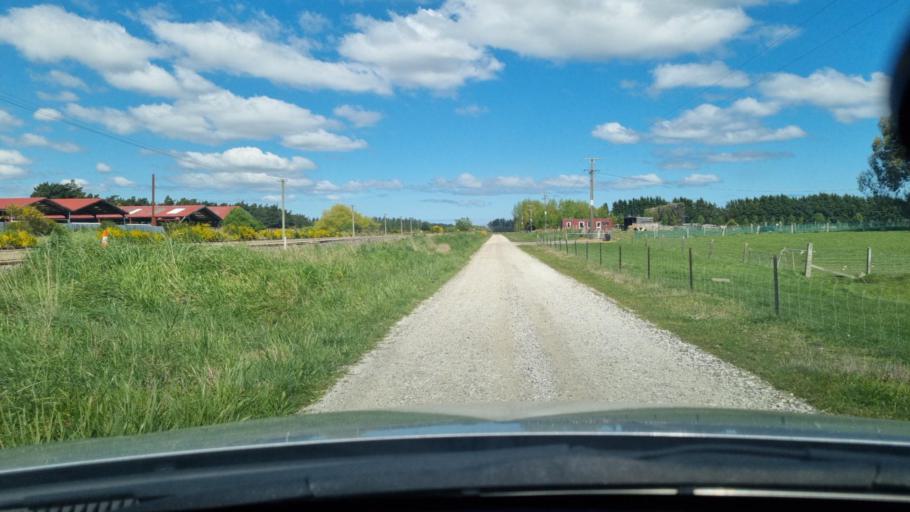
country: NZ
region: Southland
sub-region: Invercargill City
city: Invercargill
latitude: -46.3462
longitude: 168.3401
